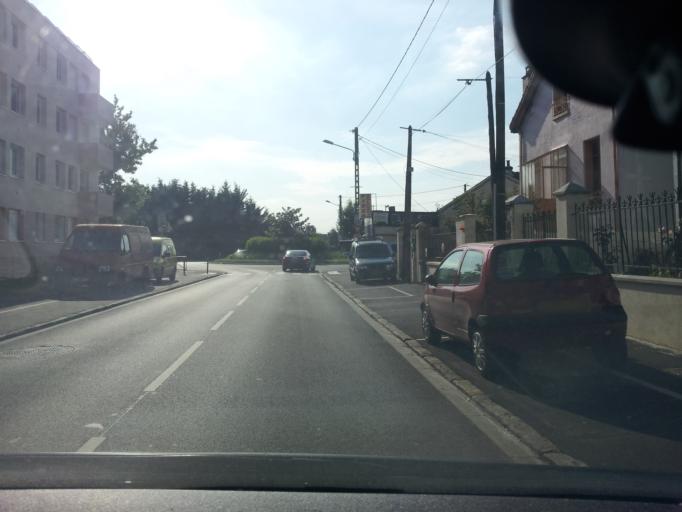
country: FR
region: Ile-de-France
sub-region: Departement de l'Essonne
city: Le Plessis-Pate
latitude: 48.6296
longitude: 2.3340
